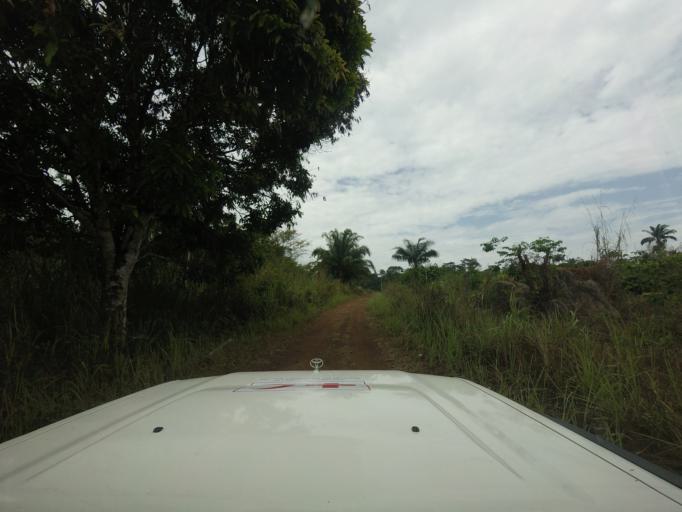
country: SL
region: Eastern Province
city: Buedu
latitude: 8.2640
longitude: -10.2416
